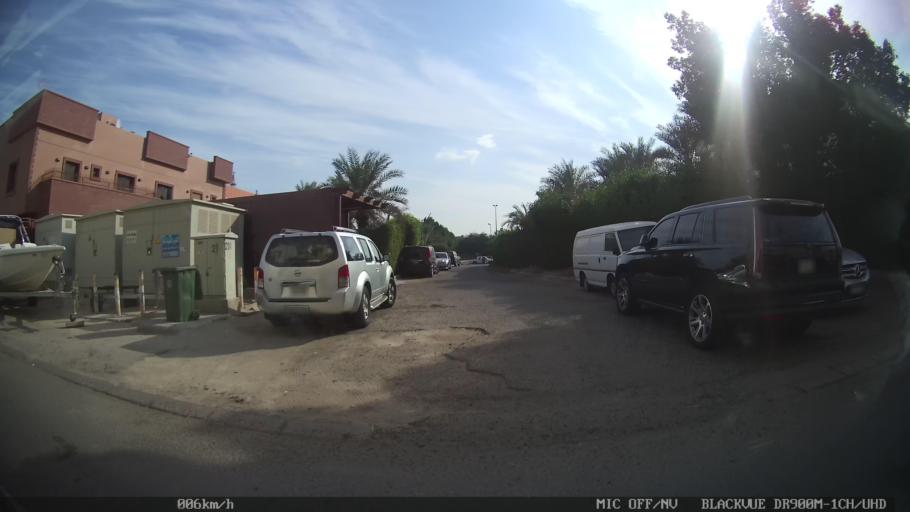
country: KW
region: Al Asimah
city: Ash Shamiyah
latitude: 29.3348
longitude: 47.9559
